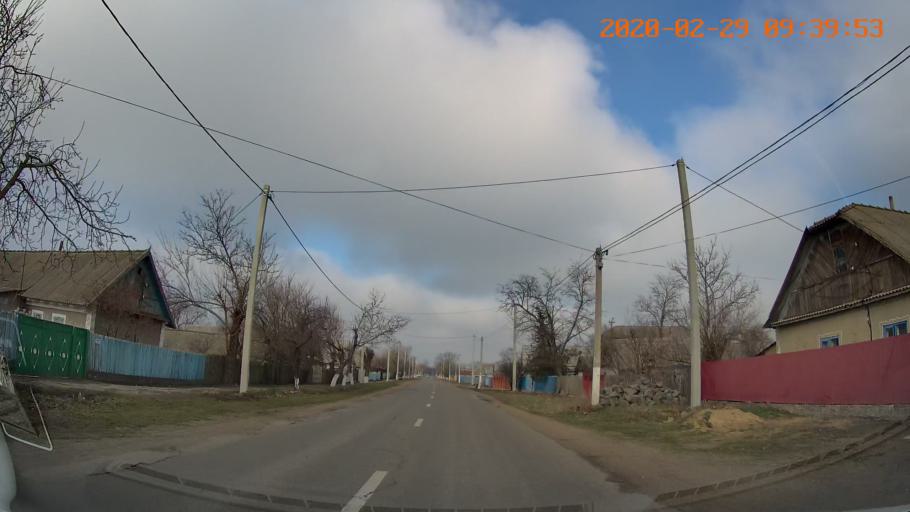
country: MD
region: Telenesti
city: Crasnoe
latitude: 46.6376
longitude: 29.8497
